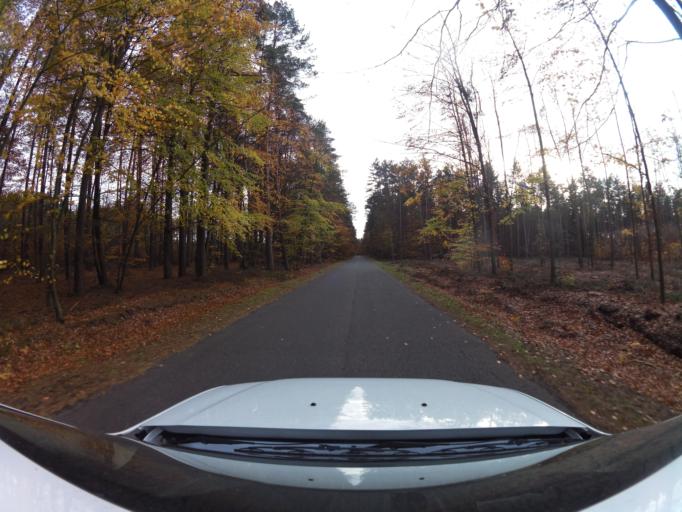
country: PL
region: West Pomeranian Voivodeship
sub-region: Powiat goleniowski
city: Nowogard
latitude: 53.7951
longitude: 15.1279
